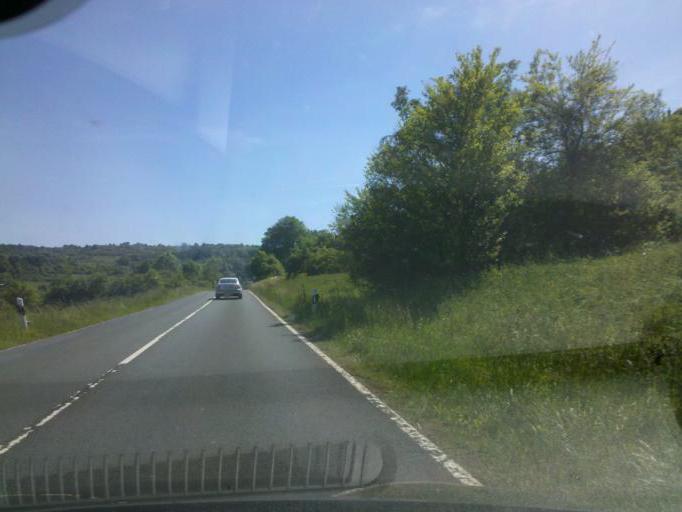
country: DE
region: Hesse
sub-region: Regierungsbezirk Giessen
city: Haiger
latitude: 50.7243
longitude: 8.1883
